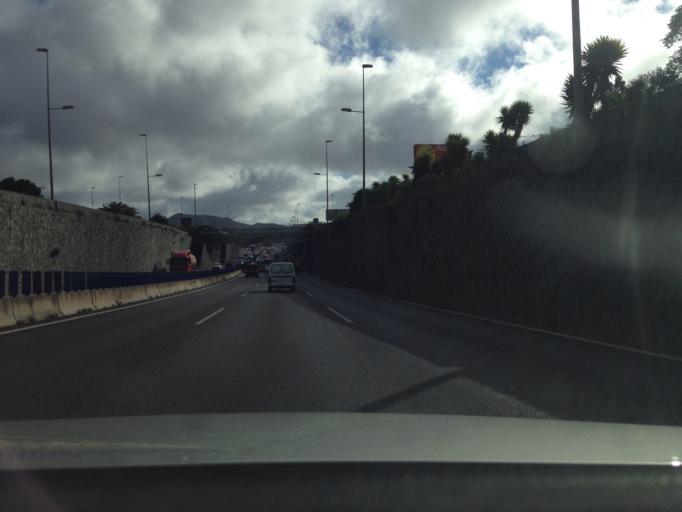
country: ES
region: Canary Islands
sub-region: Provincia de Santa Cruz de Tenerife
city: La Laguna
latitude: 28.4894
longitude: -16.3400
